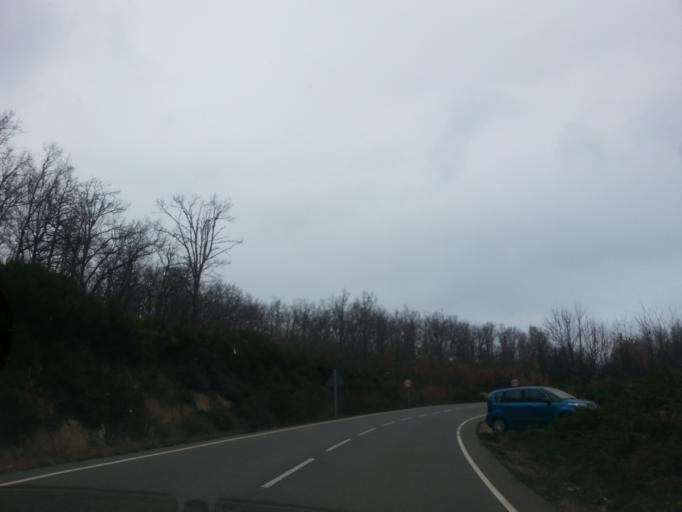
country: ES
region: Castille and Leon
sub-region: Provincia de Salamanca
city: Madronal
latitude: 40.4736
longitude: -6.0805
